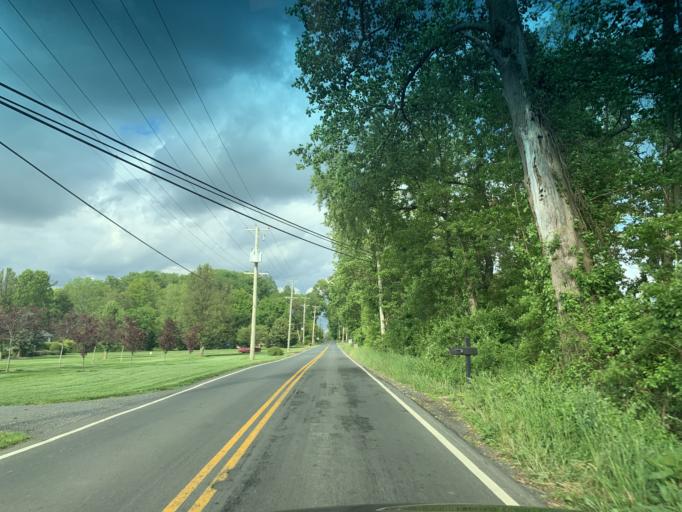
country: US
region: Maryland
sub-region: Cecil County
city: Rising Sun
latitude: 39.6860
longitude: -76.1760
